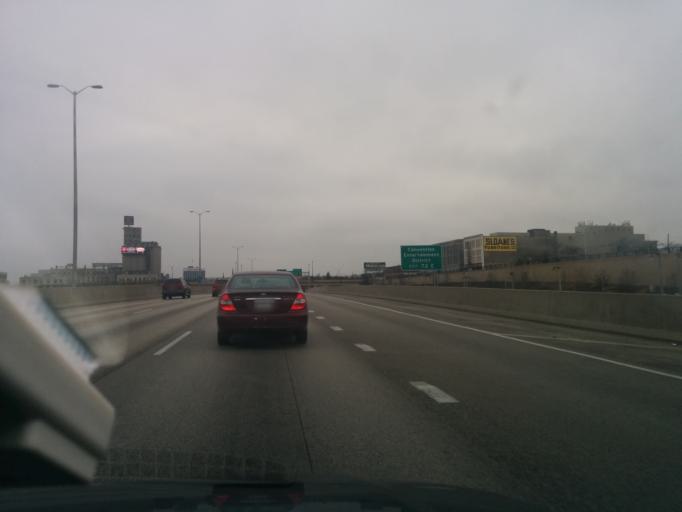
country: US
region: Wisconsin
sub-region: Milwaukee County
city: Milwaukee
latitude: 43.0514
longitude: -87.9256
